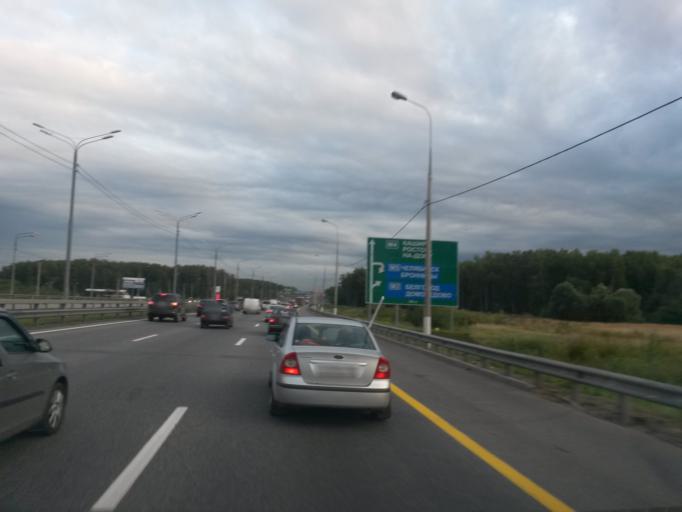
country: RU
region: Moskovskaya
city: Belyye Stolby
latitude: 55.3475
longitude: 37.8067
